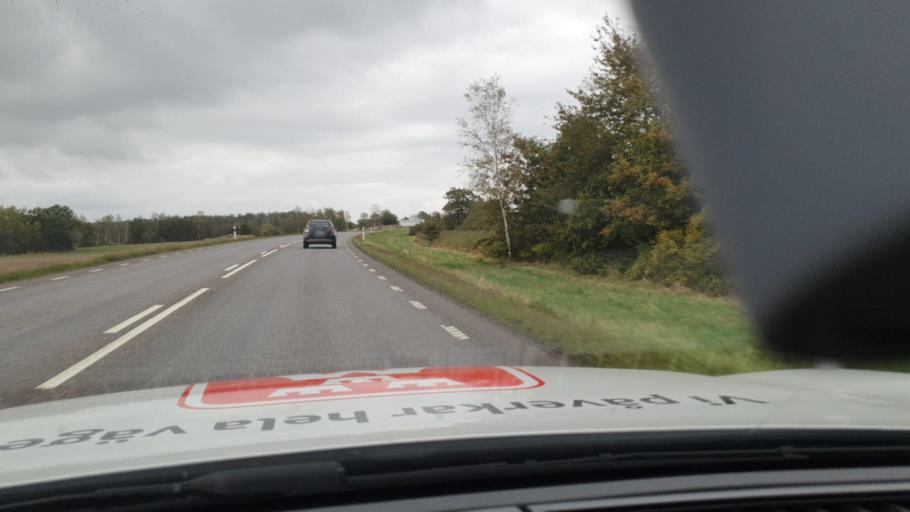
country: SE
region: Halland
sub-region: Falkenbergs Kommun
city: Falkenberg
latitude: 56.9574
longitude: 12.5458
